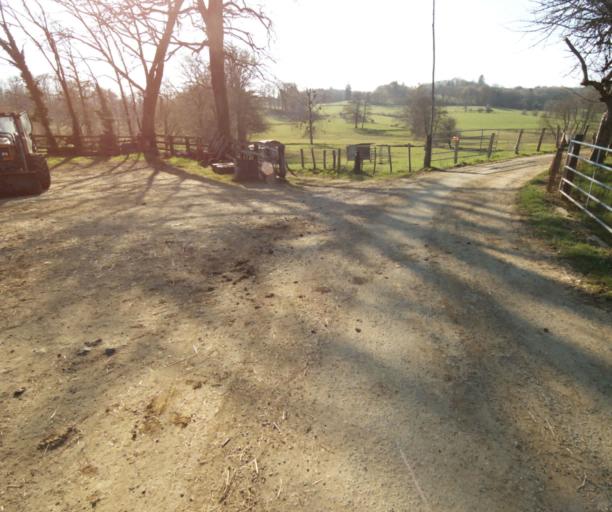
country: FR
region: Limousin
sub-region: Departement de la Correze
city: Saint-Clement
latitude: 45.3388
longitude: 1.6685
